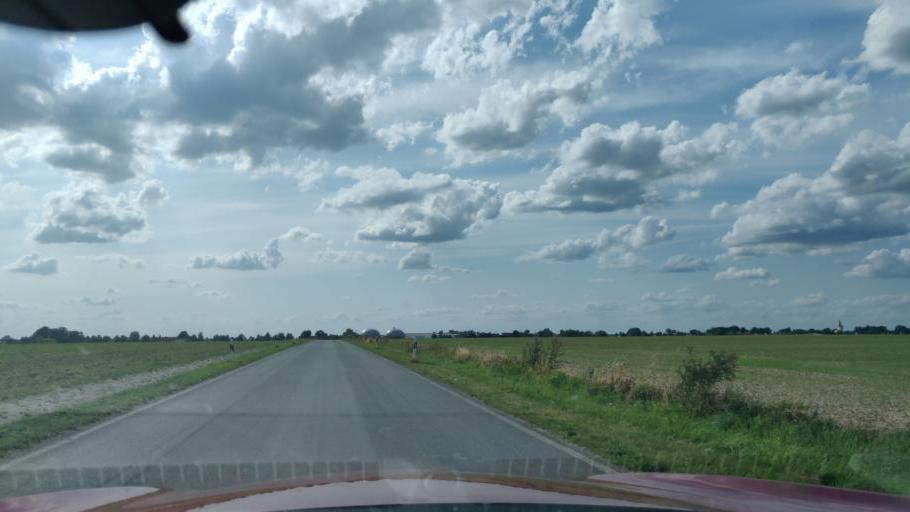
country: DE
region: Saxony
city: Schildau
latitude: 51.4822
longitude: 12.9210
